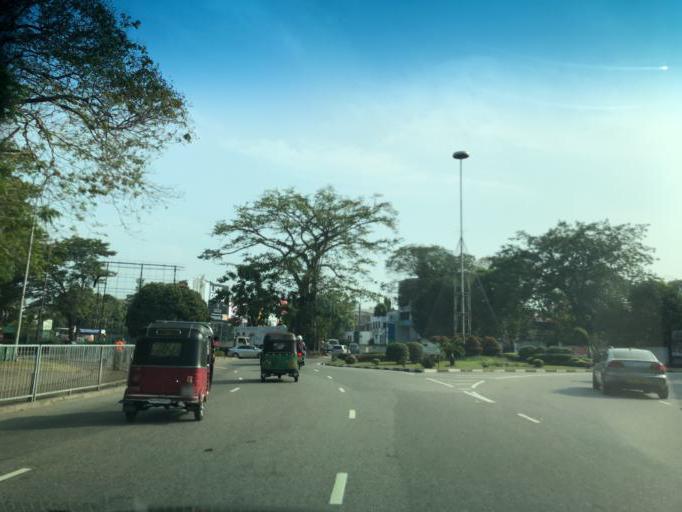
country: LK
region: Western
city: Colombo
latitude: 6.9125
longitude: 79.8579
